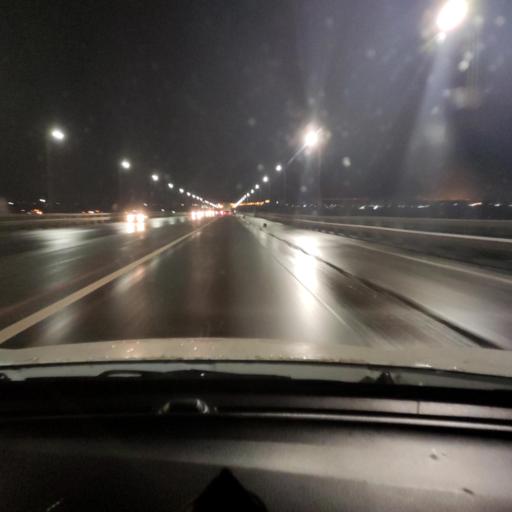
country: RU
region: Tatarstan
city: Osinovo
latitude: 55.7838
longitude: 48.8405
